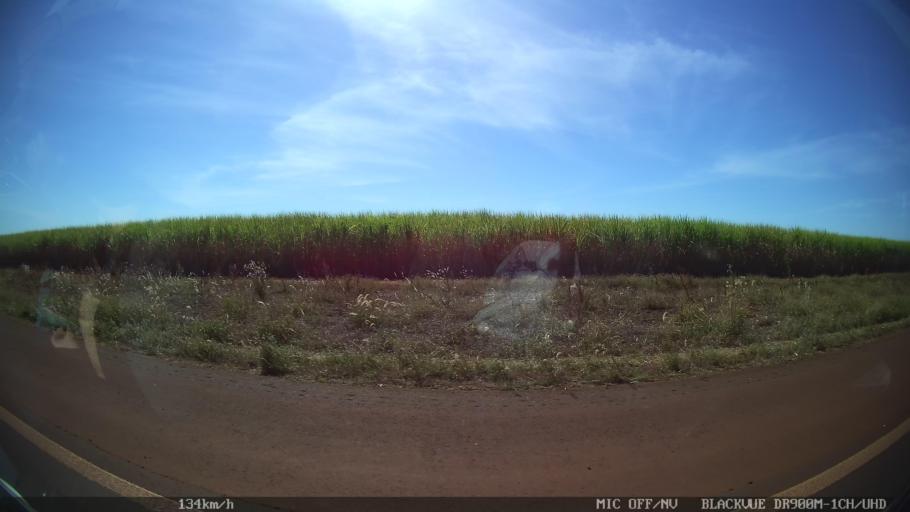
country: BR
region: Sao Paulo
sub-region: Guaira
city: Guaira
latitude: -20.4439
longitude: -48.3502
